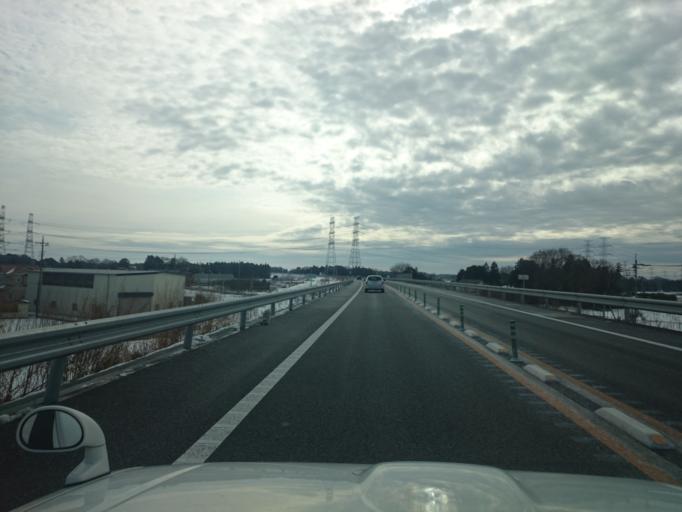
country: JP
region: Ibaraki
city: Sakai
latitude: 36.1199
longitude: 139.8331
